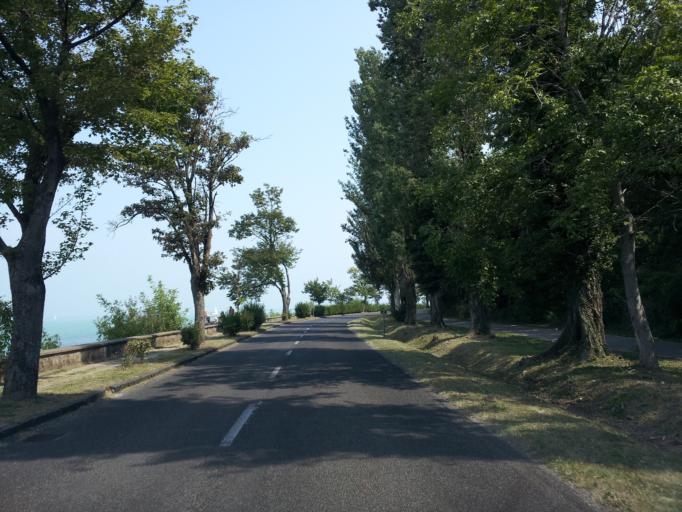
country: HU
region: Veszprem
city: Tihany
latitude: 46.9239
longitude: 17.8828
